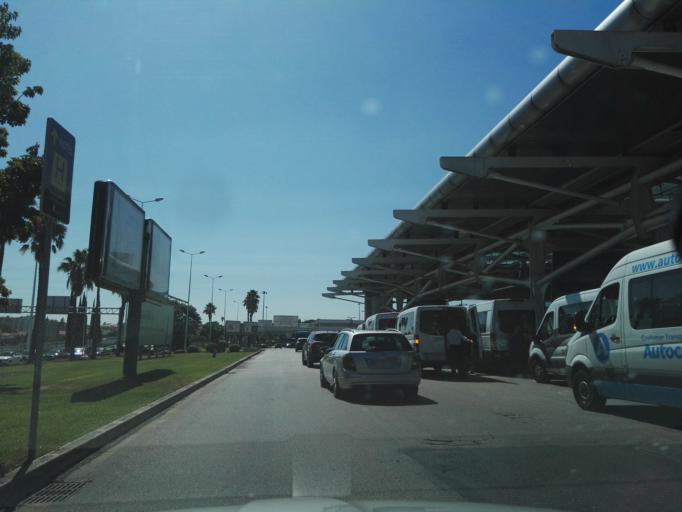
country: PT
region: Lisbon
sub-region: Loures
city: Moscavide
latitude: 38.7702
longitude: -9.1281
